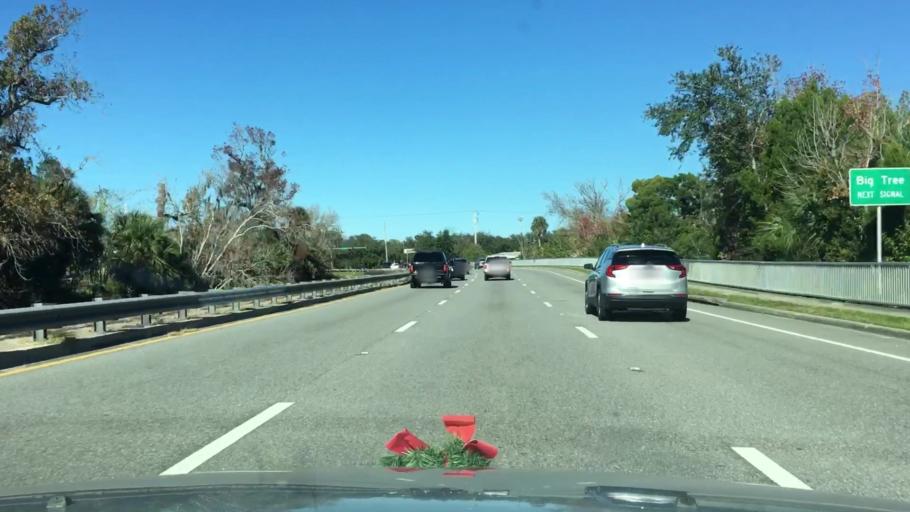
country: US
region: Florida
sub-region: Volusia County
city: South Daytona
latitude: 29.1645
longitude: -81.0231
